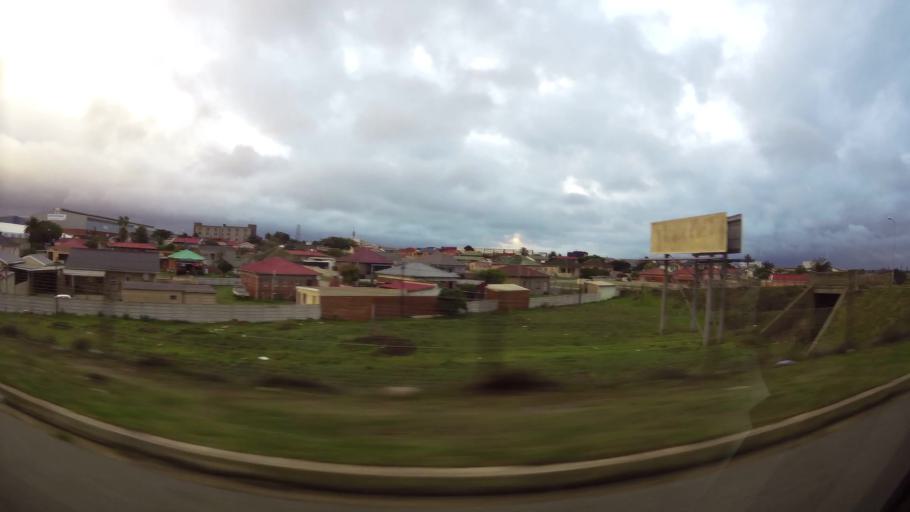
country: ZA
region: Eastern Cape
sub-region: Nelson Mandela Bay Metropolitan Municipality
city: Port Elizabeth
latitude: -33.9258
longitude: 25.6048
